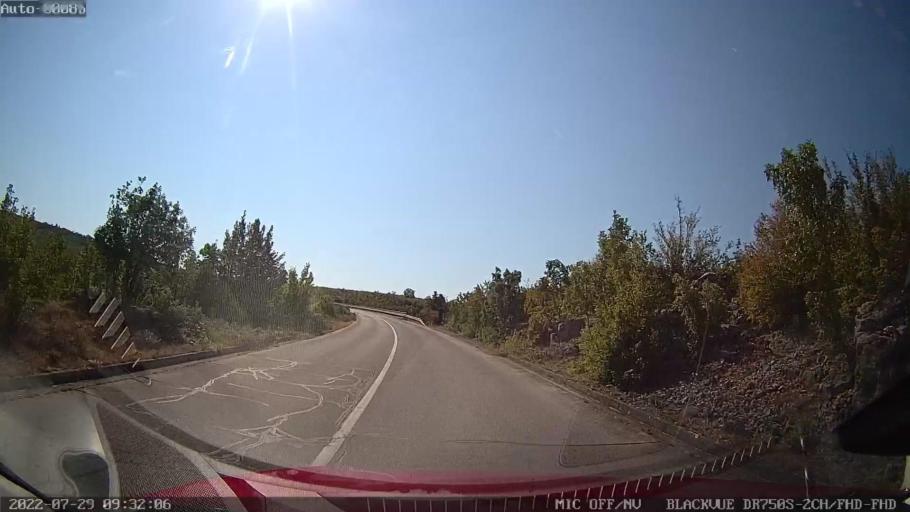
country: HR
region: Zadarska
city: Obrovac
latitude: 44.1841
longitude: 15.7066
